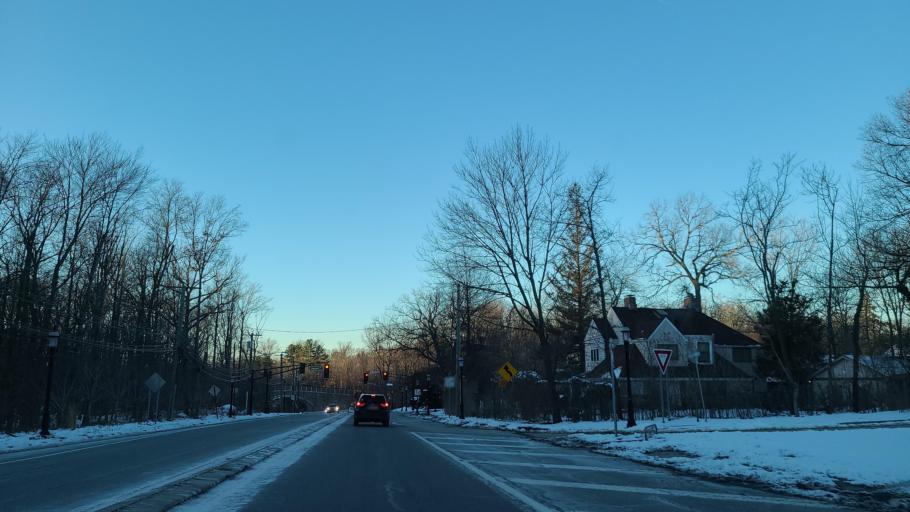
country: US
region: New Jersey
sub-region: Essex County
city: Maplewood
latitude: 40.7469
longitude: -74.2822
